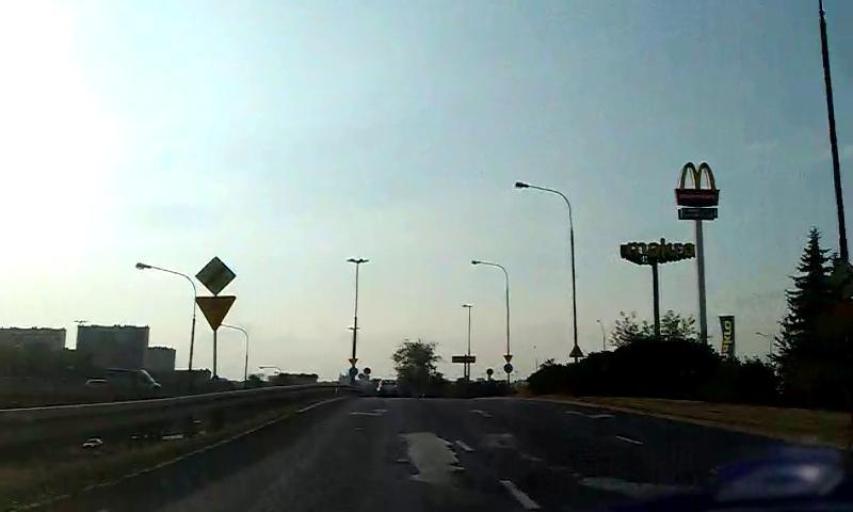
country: PL
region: Lublin Voivodeship
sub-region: Powiat lubelski
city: Lublin
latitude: 51.2361
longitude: 22.5976
